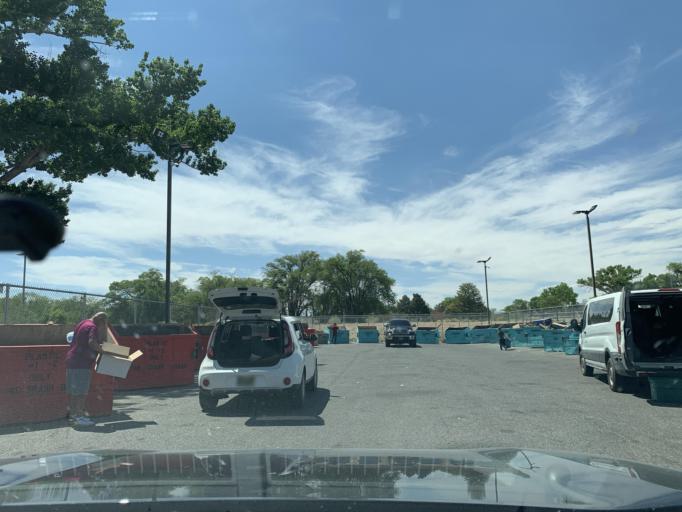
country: US
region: New Mexico
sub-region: Valencia County
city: Los Lunas
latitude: 34.8137
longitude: -106.7400
